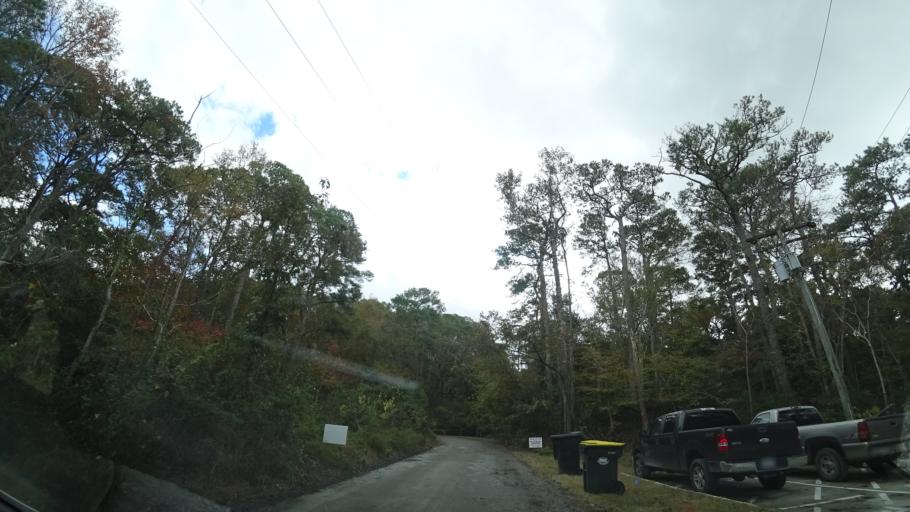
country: US
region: North Carolina
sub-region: Dare County
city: Kill Devil Hills
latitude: 35.9900
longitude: -75.6645
